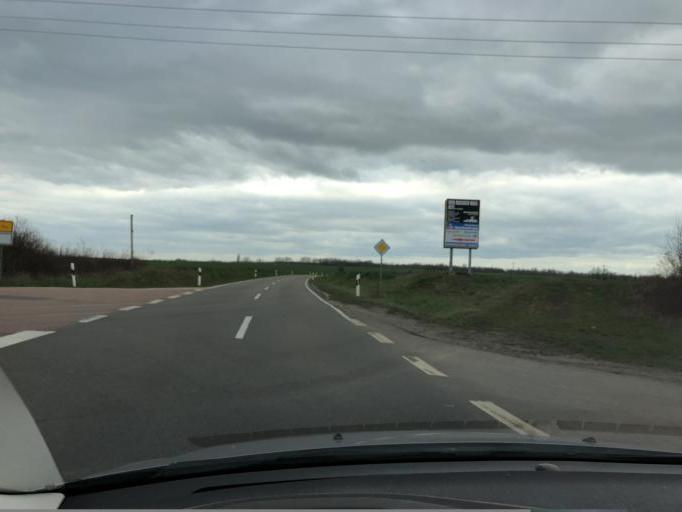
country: DE
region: Saxony-Anhalt
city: Hohenmolsen
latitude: 51.1500
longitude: 12.1303
